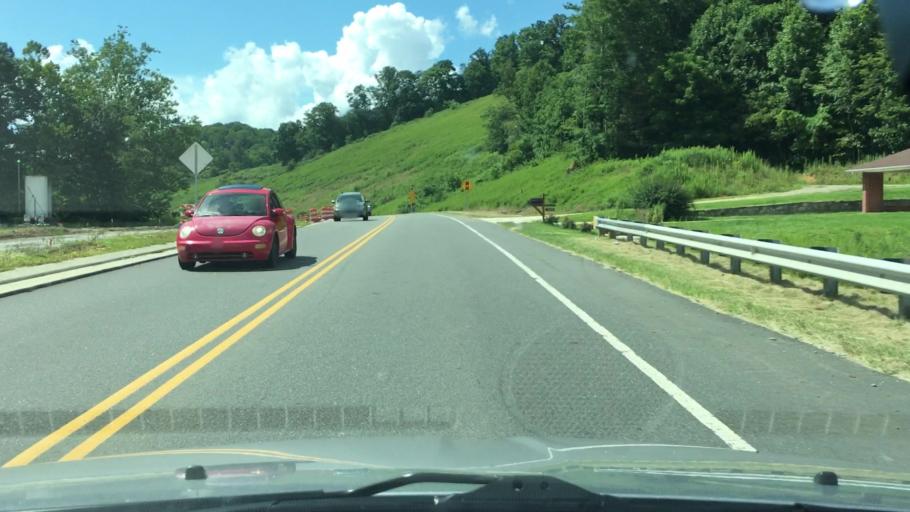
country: US
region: North Carolina
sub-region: Yancey County
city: Burnsville
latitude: 35.9099
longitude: -82.2201
